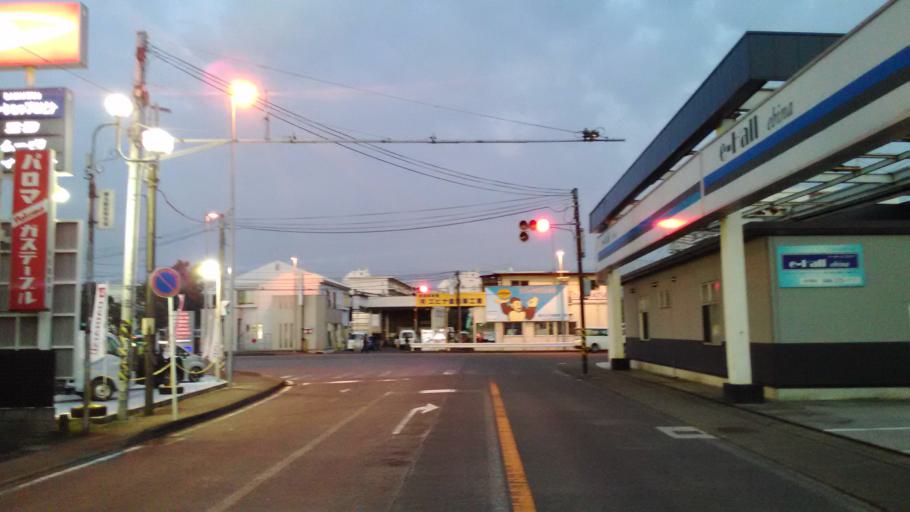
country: JP
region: Kanagawa
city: Atsugi
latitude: 35.4448
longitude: 139.3774
